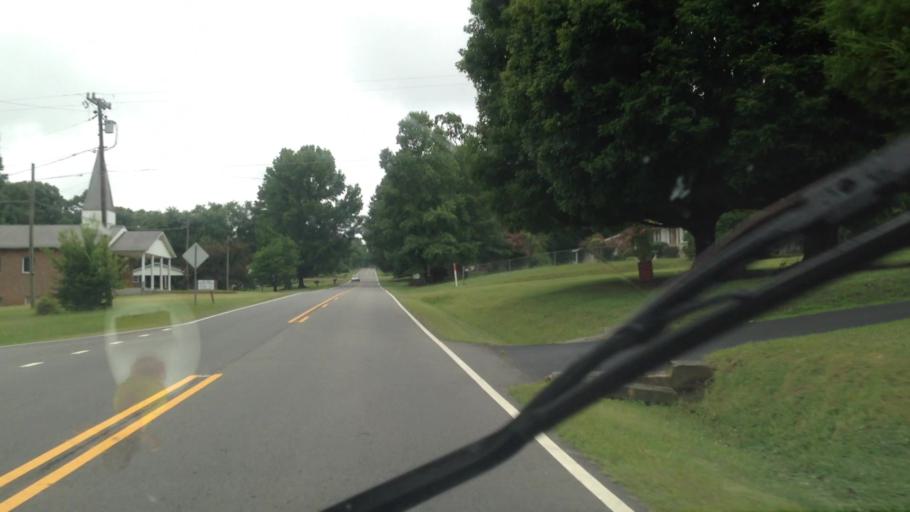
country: US
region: North Carolina
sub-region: Rockingham County
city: Mayodan
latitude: 36.4096
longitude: -79.9937
